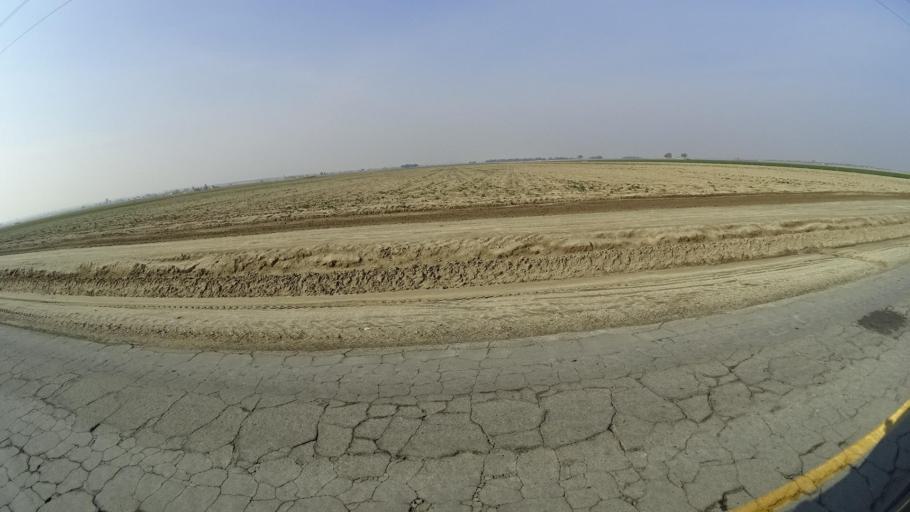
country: US
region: California
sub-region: Kern County
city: Arvin
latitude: 35.0662
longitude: -118.8466
